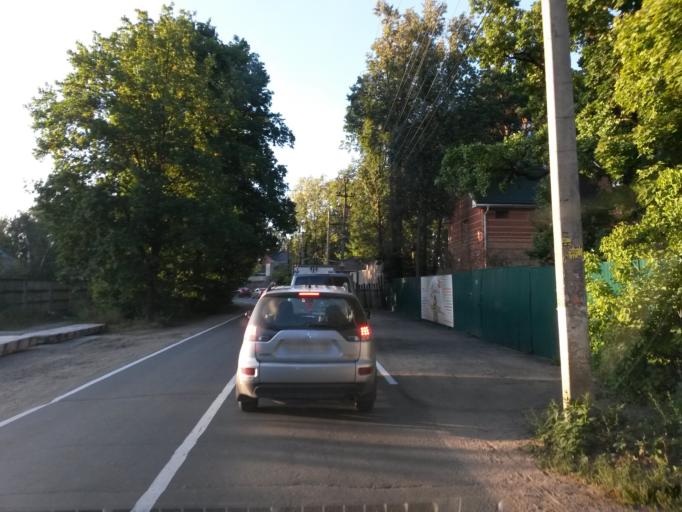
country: RU
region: Moskovskaya
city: Mamontovka
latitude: 55.9700
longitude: 37.8280
